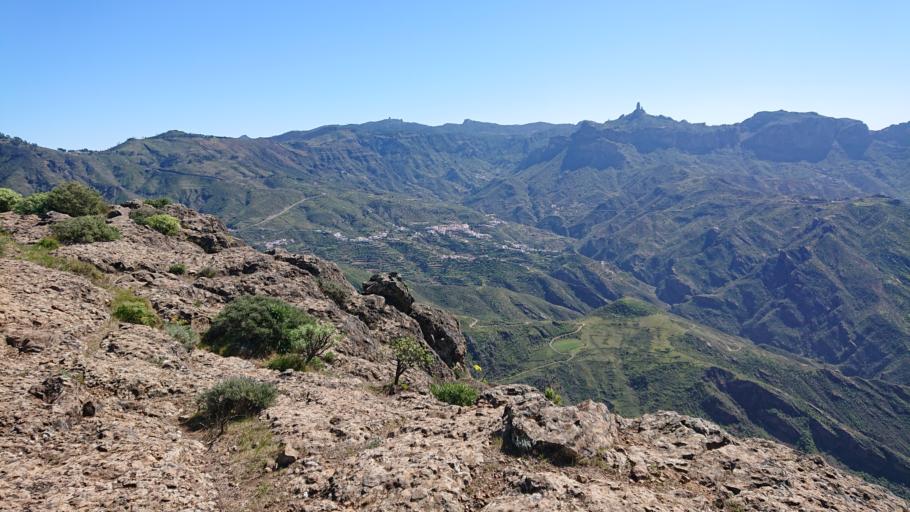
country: ES
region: Canary Islands
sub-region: Provincia de Las Palmas
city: Artenara
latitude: 28.0174
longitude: -15.6370
